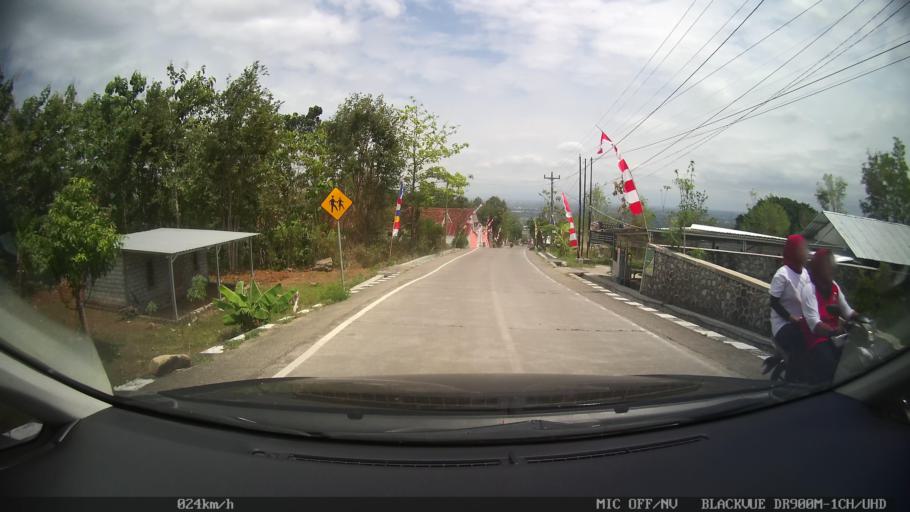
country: ID
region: Central Java
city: Candi Prambanan
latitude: -7.7836
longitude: 110.5054
